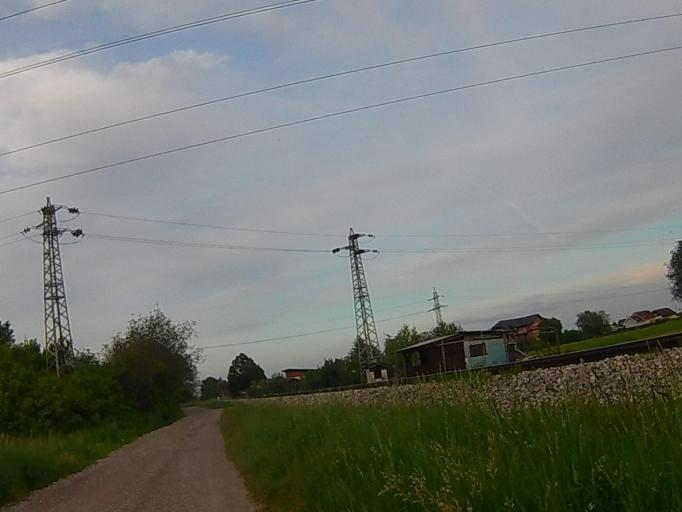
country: SI
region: Maribor
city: Pekre
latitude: 46.5589
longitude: 15.5997
